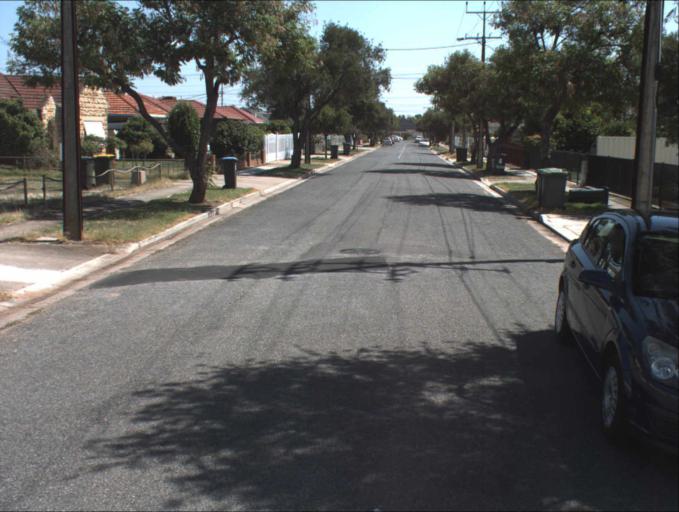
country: AU
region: South Australia
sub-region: Charles Sturt
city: Woodville
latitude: -34.8821
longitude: 138.5705
